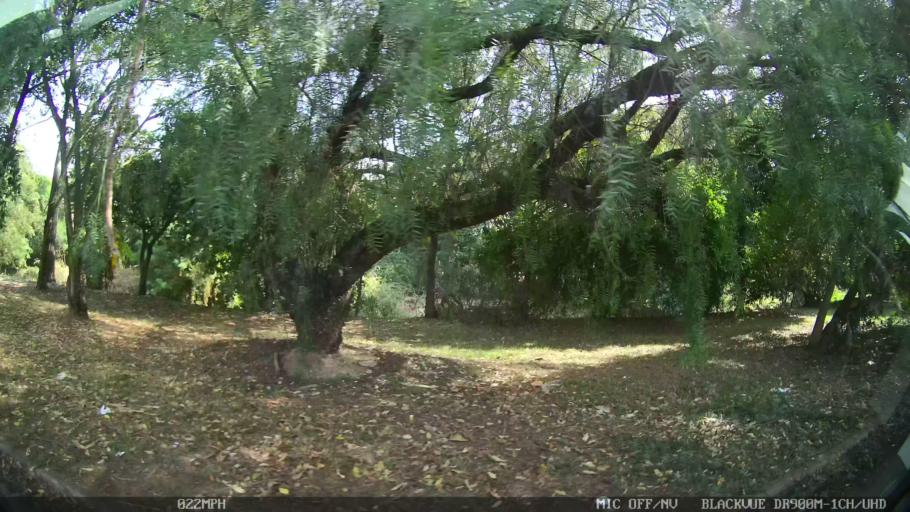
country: BR
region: Sao Paulo
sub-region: Piracicaba
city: Piracicaba
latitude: -22.7262
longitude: -47.6715
